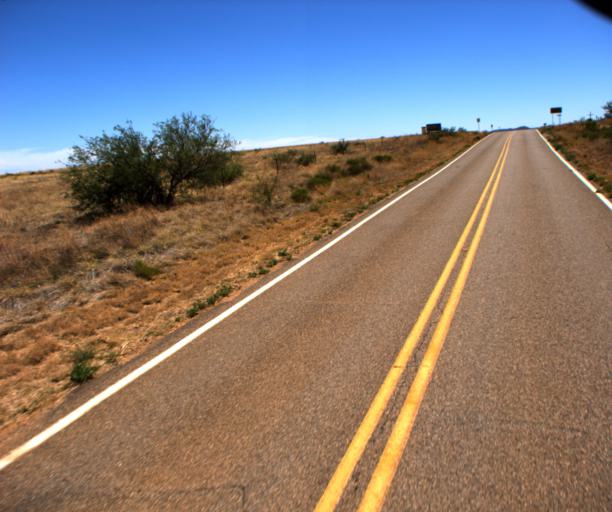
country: US
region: Arizona
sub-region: Pima County
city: Sells
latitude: 31.5904
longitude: -111.5307
